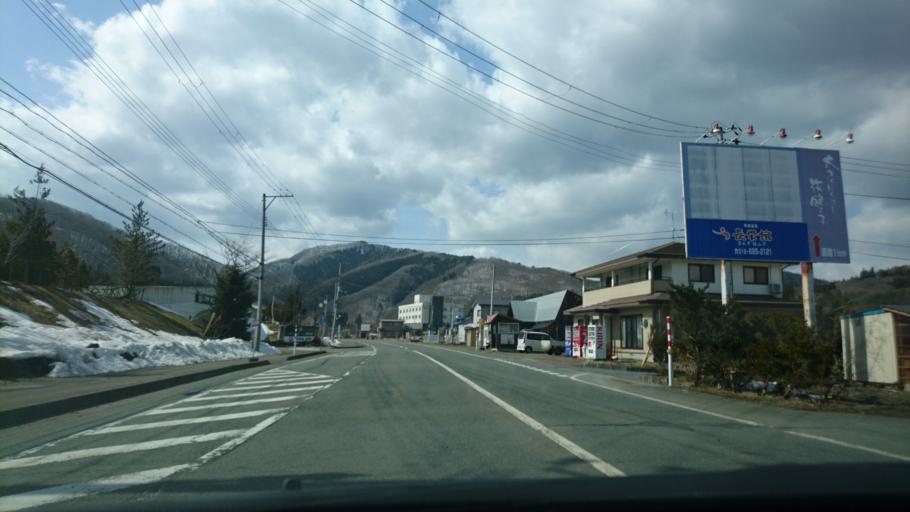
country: JP
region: Iwate
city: Shizukuishi
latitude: 39.6413
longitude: 140.9343
